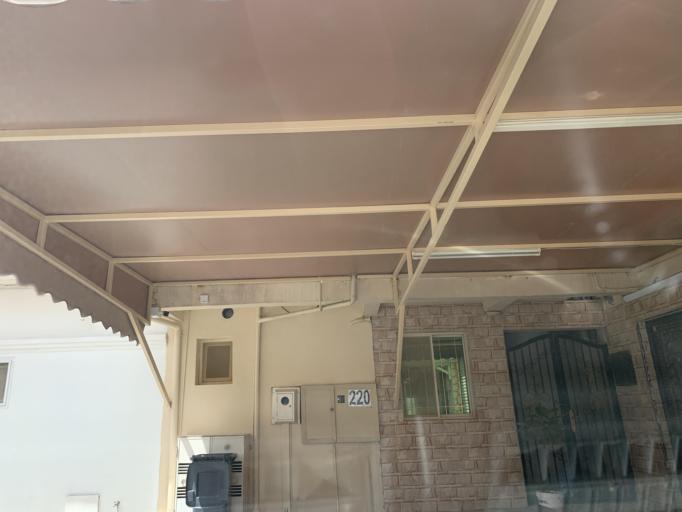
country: BH
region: Northern
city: Ar Rifa'
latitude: 26.1422
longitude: 50.5653
